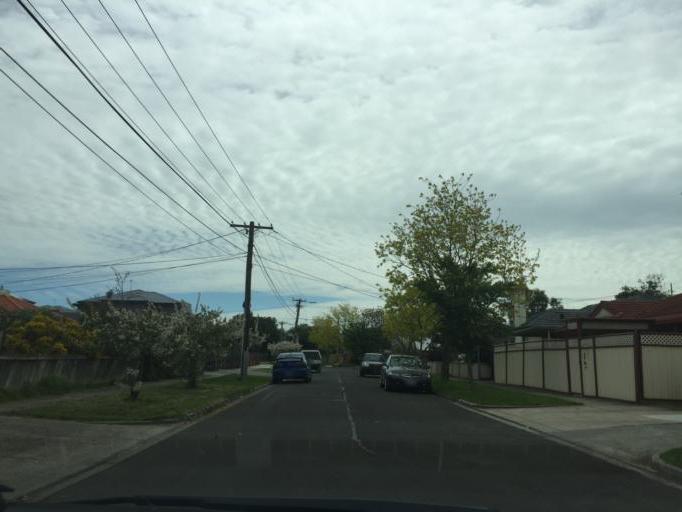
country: AU
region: Victoria
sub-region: Maribyrnong
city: Maidstone
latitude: -37.7845
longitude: 144.8756
